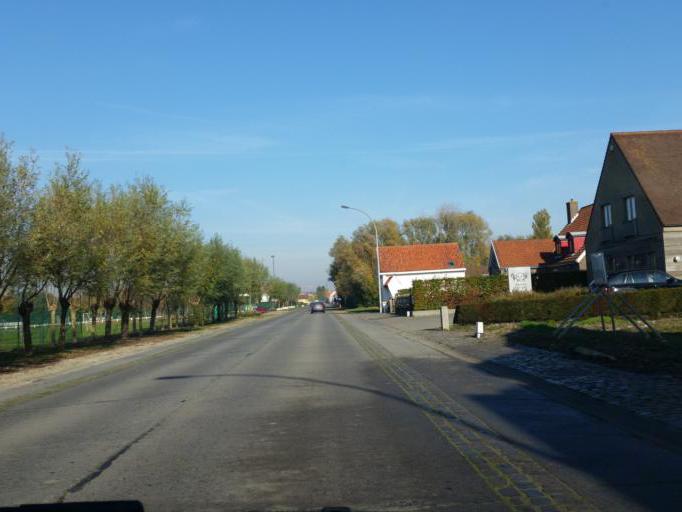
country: BE
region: Flanders
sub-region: Provincie West-Vlaanderen
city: De Haan
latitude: 51.2602
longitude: 3.0300
